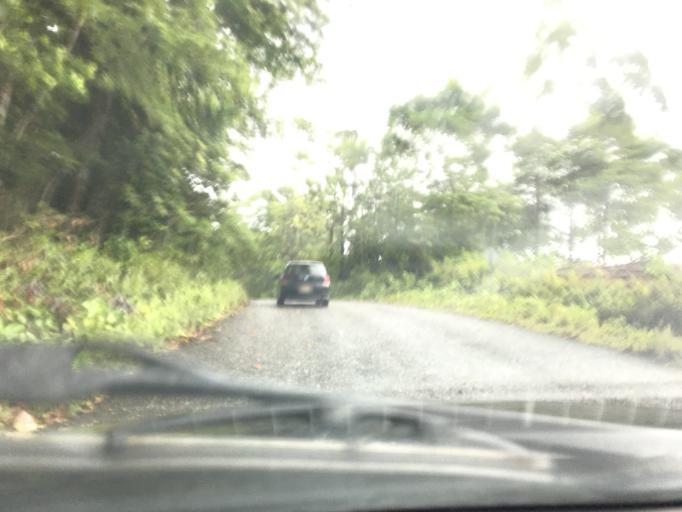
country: SB
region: Western Province
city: Gizo
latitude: -8.2976
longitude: 157.2525
